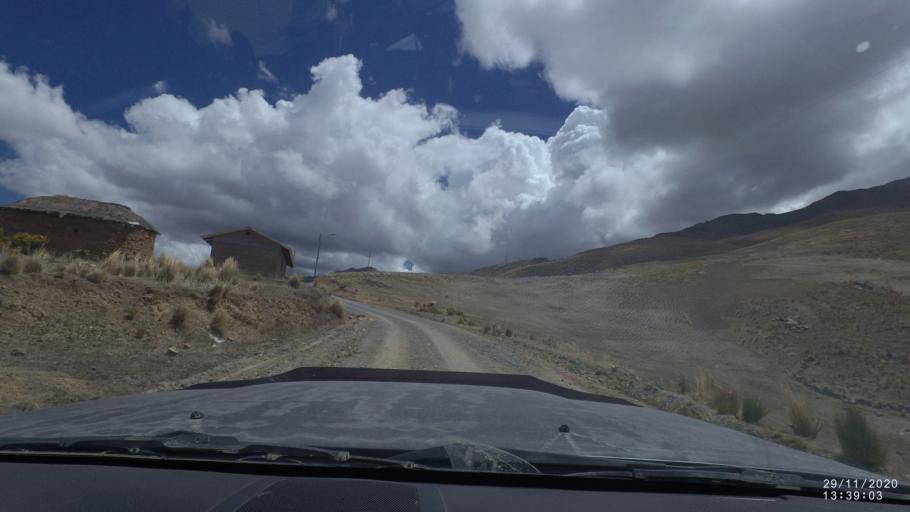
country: BO
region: Cochabamba
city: Cochabamba
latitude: -17.1220
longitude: -66.3278
